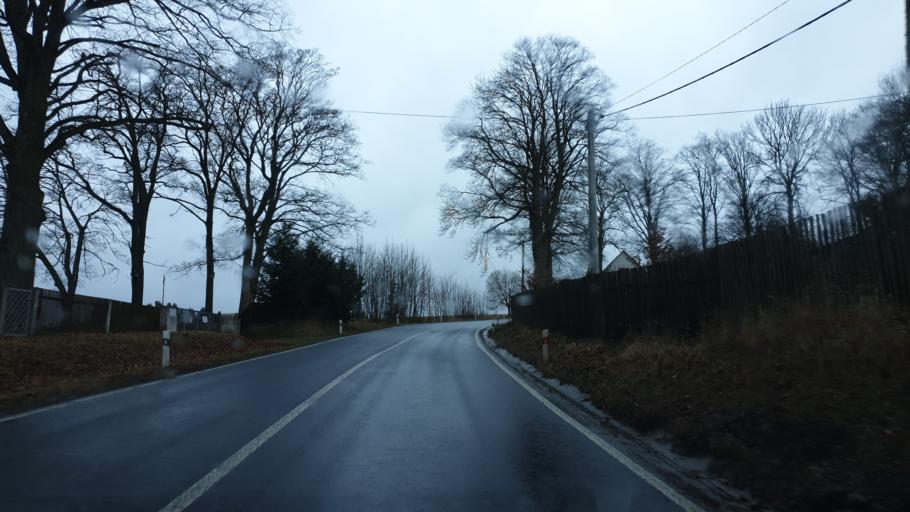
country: CZ
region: Karlovarsky
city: Hranice
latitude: 50.2749
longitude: 12.1880
